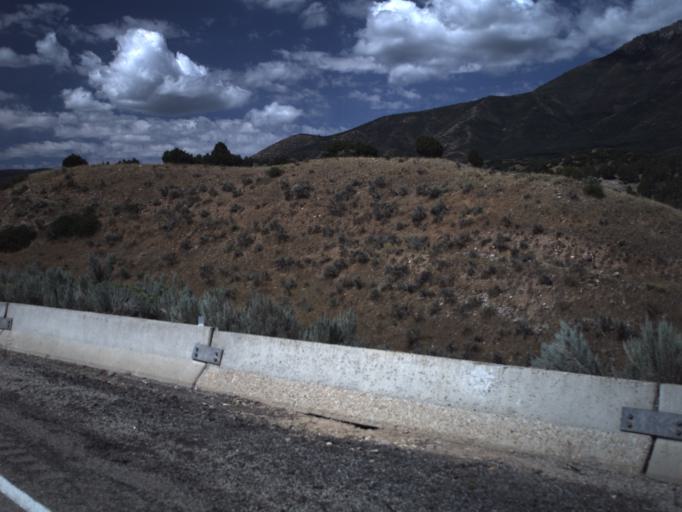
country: US
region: Utah
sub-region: Utah County
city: Woodland Hills
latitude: 39.9512
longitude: -111.5333
